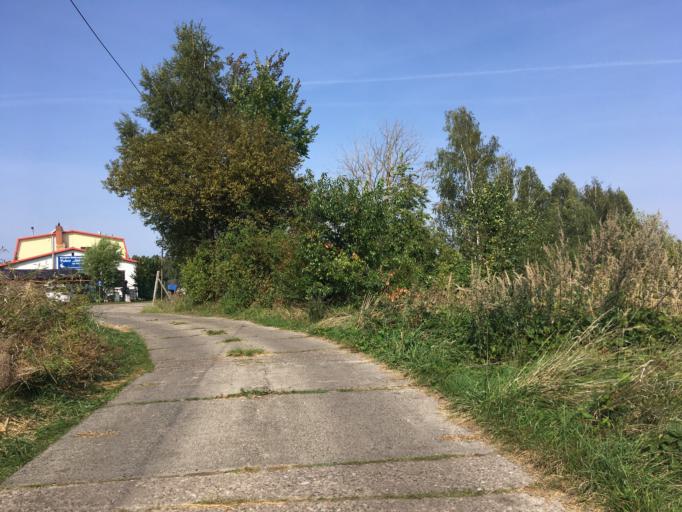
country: DE
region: Brandenburg
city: Erkner
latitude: 52.3970
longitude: 13.7333
